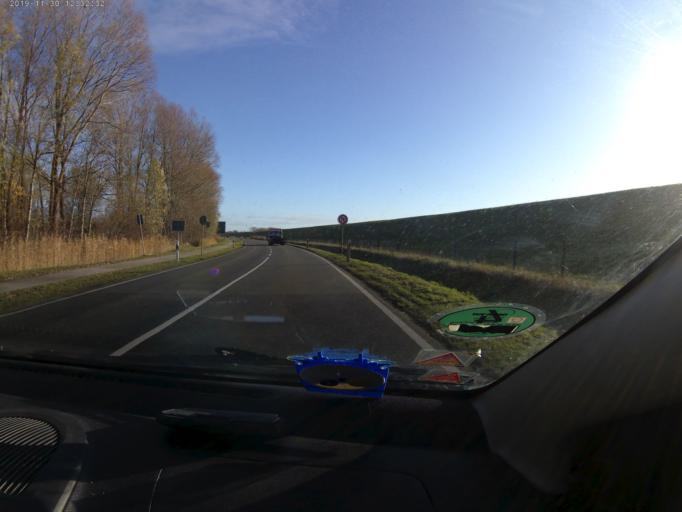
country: DE
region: Lower Saxony
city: Jemgum
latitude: 53.2347
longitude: 7.4111
